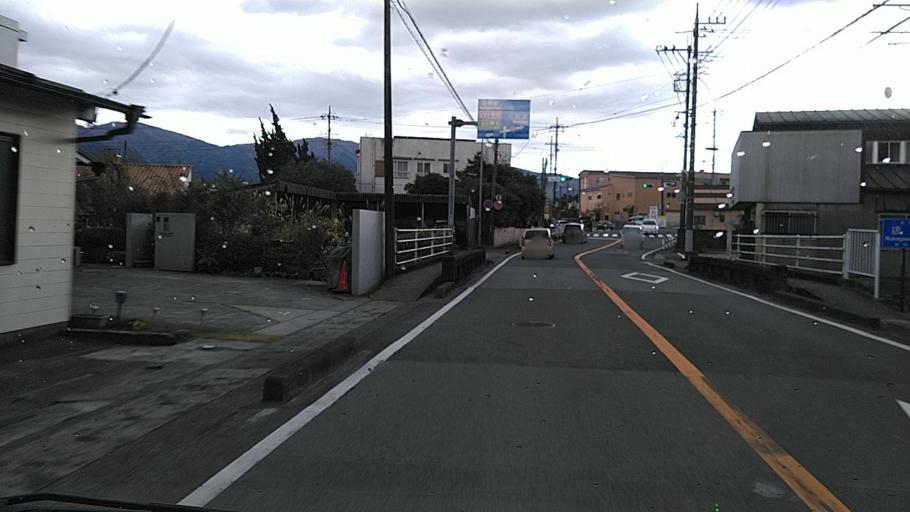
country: JP
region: Shizuoka
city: Gotemba
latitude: 35.3175
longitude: 138.9428
